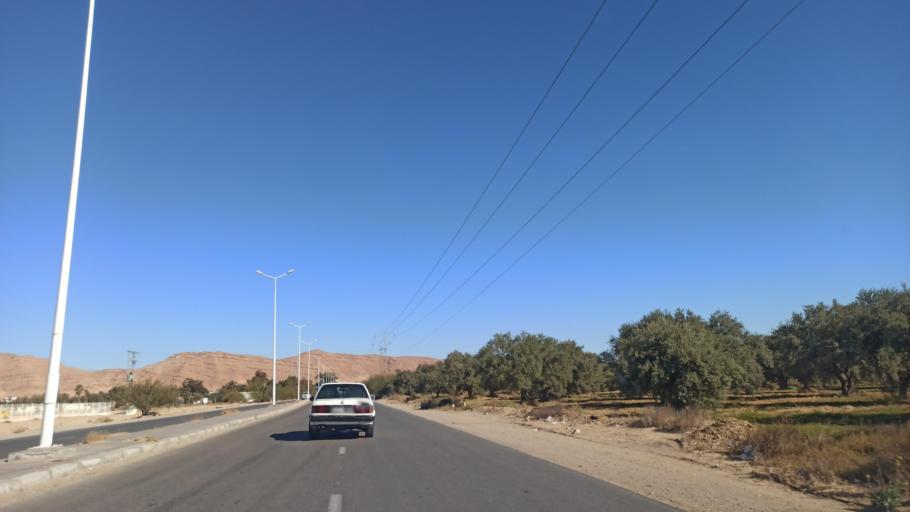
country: TN
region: Gafsa
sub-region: Gafsa Municipality
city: Gafsa
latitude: 34.4155
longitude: 8.7414
